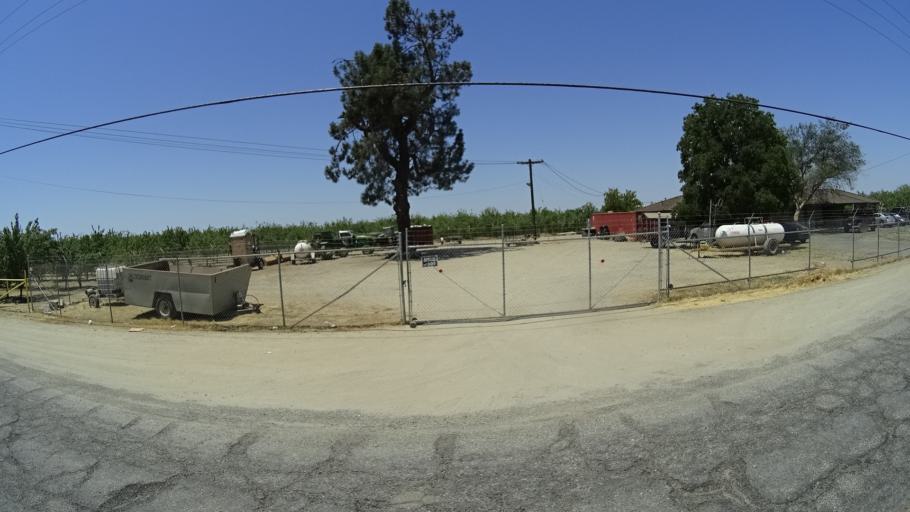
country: US
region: California
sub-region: Fresno County
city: West Park
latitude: 36.7321
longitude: -119.8356
